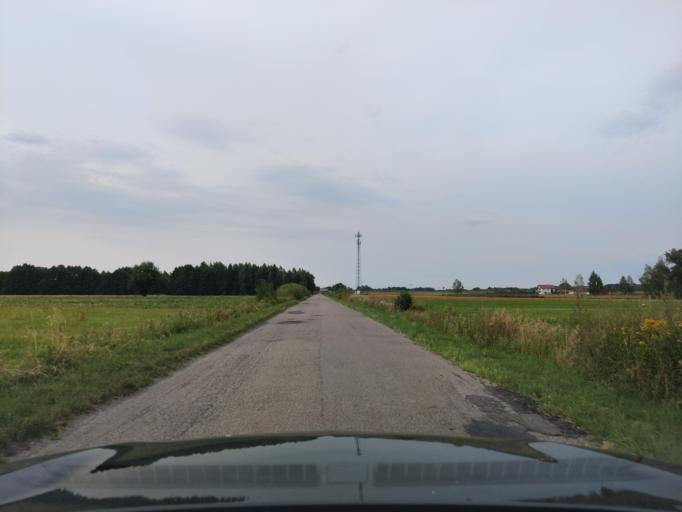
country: PL
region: Masovian Voivodeship
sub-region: Powiat pultuski
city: Obryte
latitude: 52.7314
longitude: 21.2465
